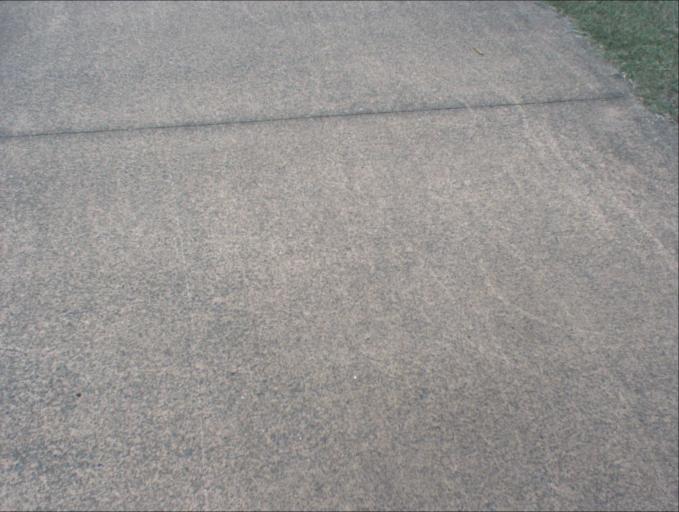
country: AU
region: Queensland
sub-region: Logan
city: Beenleigh
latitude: -27.7063
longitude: 153.1954
